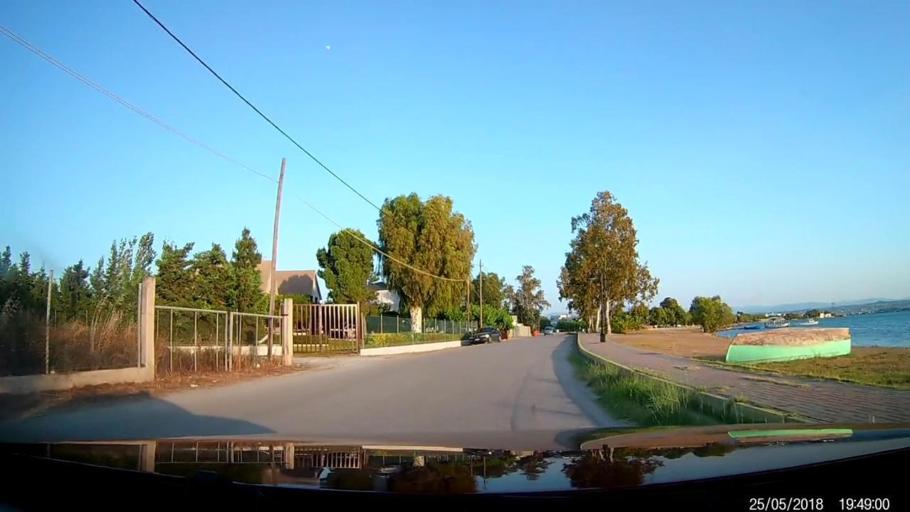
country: GR
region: Central Greece
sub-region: Nomos Evvoias
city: Ayios Nikolaos
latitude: 38.4139
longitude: 23.6407
